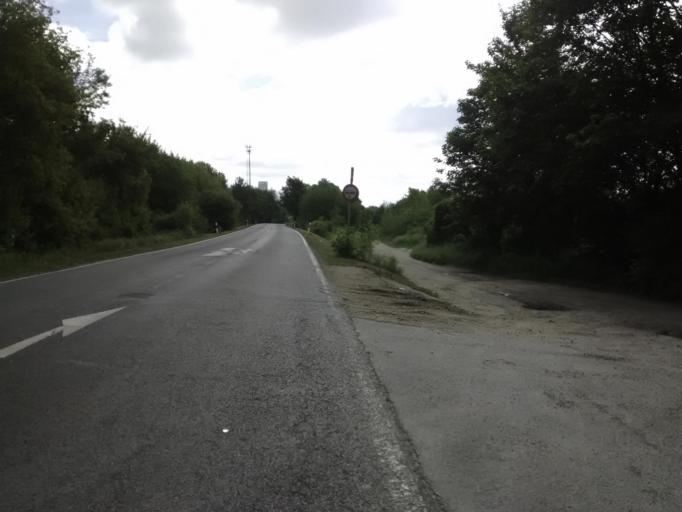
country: DE
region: Berlin
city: Blankenfelde
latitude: 52.6624
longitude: 13.4048
